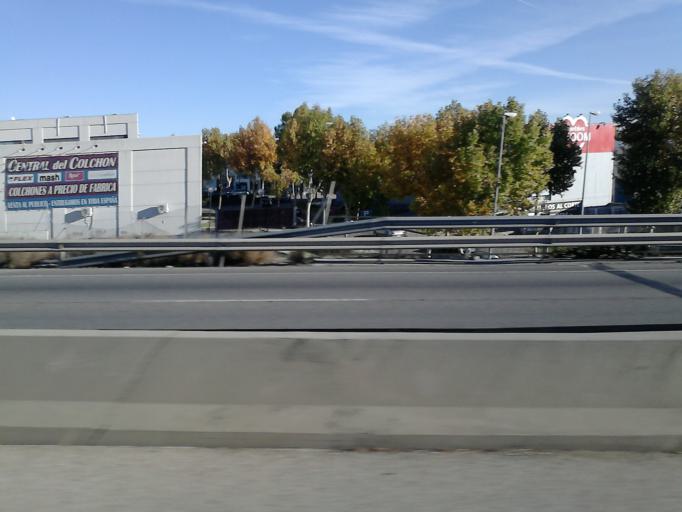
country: ES
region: Madrid
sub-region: Provincia de Madrid
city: Las Rozas de Madrid
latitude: 40.4970
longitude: -3.8903
